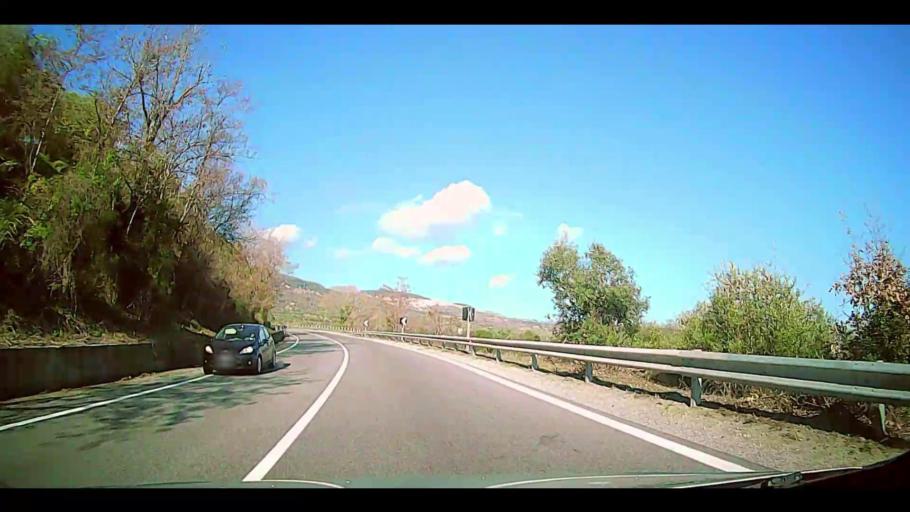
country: IT
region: Calabria
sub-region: Provincia di Crotone
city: Caccuri
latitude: 39.2072
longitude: 16.8045
